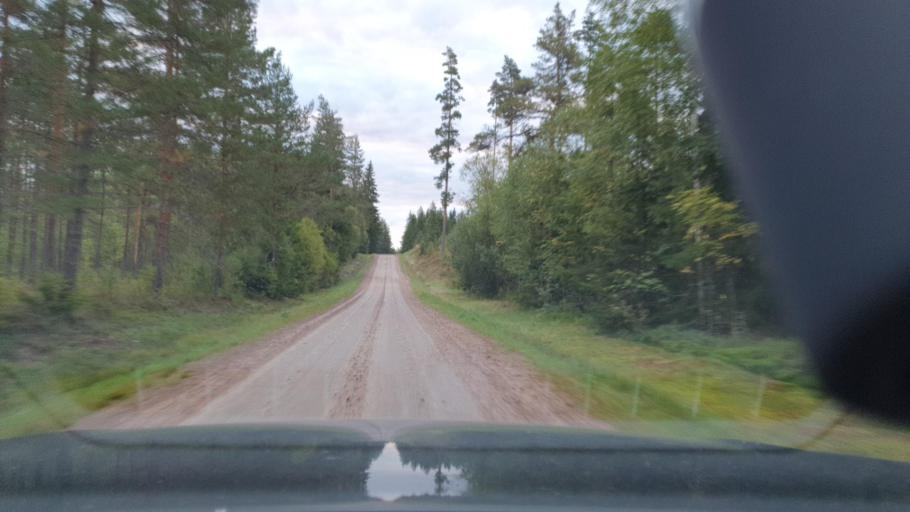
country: SE
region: Vaermland
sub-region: Munkfors Kommun
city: Munkfors
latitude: 59.8203
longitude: 13.4591
